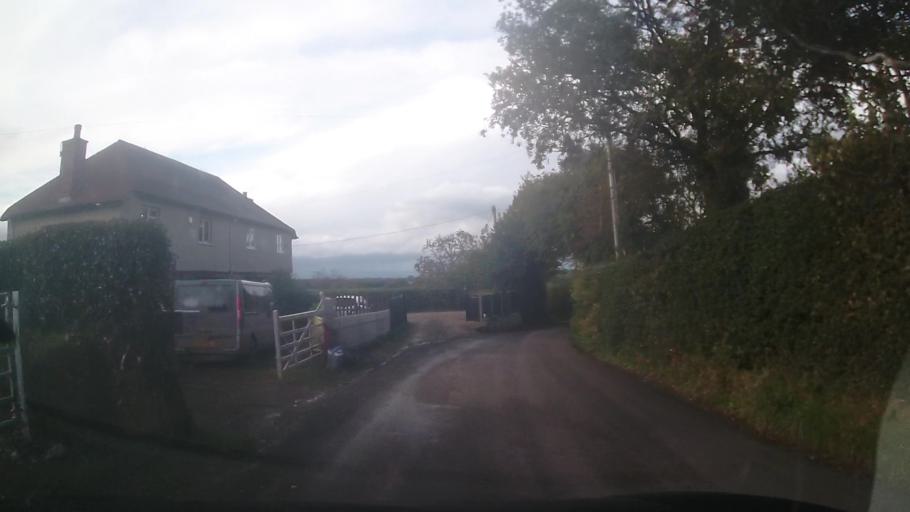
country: GB
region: England
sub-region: Shropshire
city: Whitchurch
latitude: 52.9402
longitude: -2.7160
